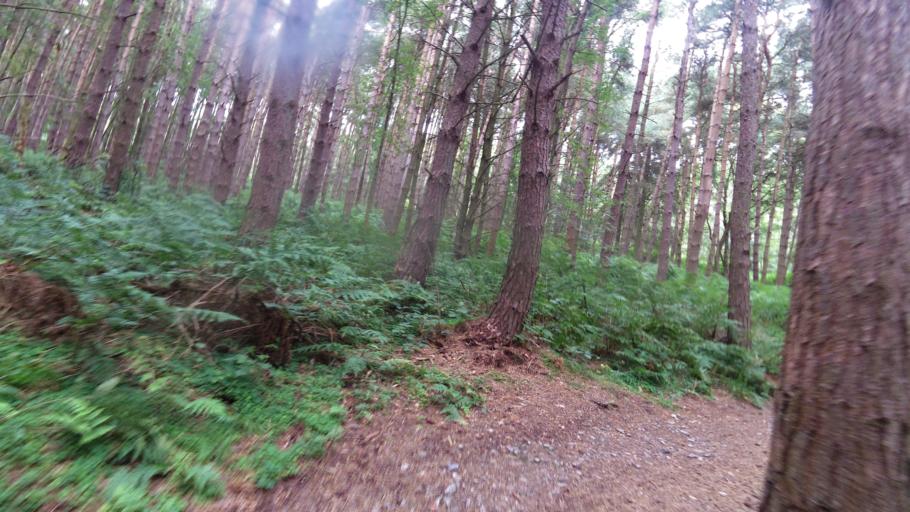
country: GB
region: England
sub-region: City and Borough of Leeds
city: Otley
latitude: 53.9560
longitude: -1.6831
